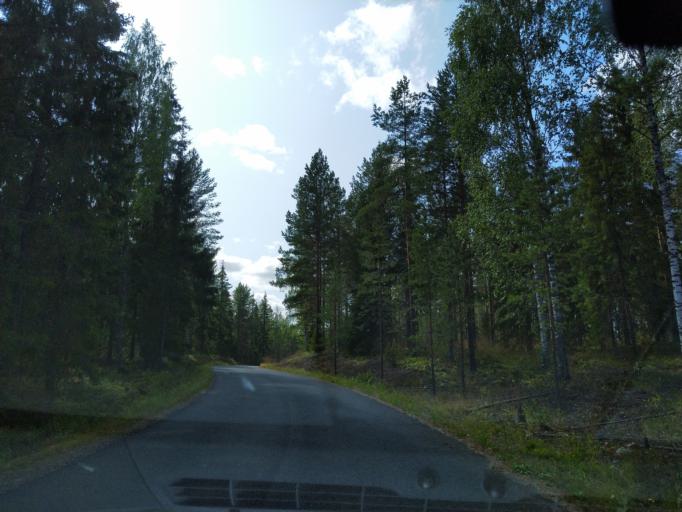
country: FI
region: Uusimaa
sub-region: Helsinki
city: Karkkila
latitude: 60.7185
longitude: 24.2061
